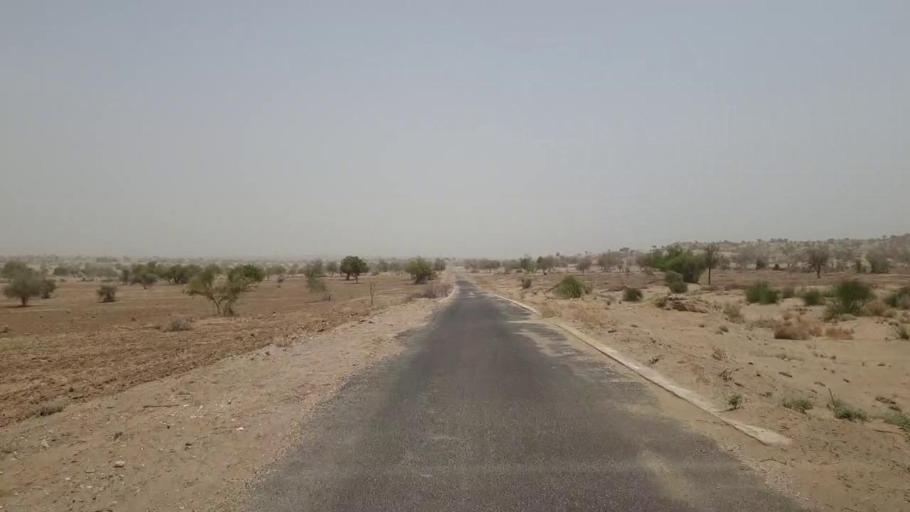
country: PK
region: Sindh
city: Islamkot
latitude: 24.8103
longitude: 70.5342
